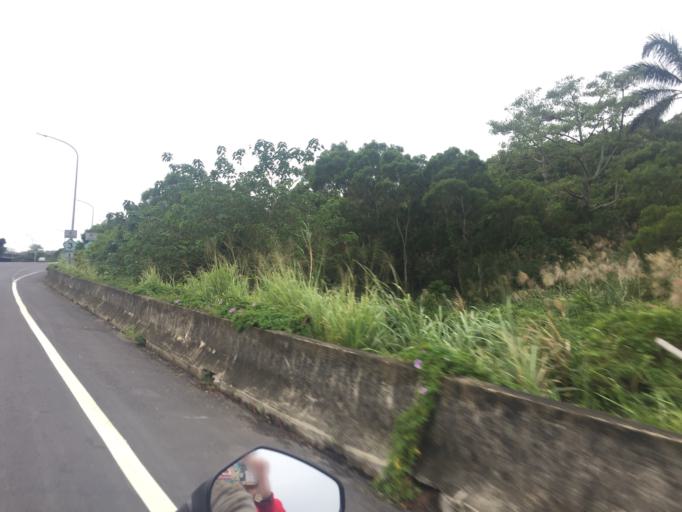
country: TW
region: Taiwan
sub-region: Hsinchu
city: Hsinchu
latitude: 24.7597
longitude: 120.9582
